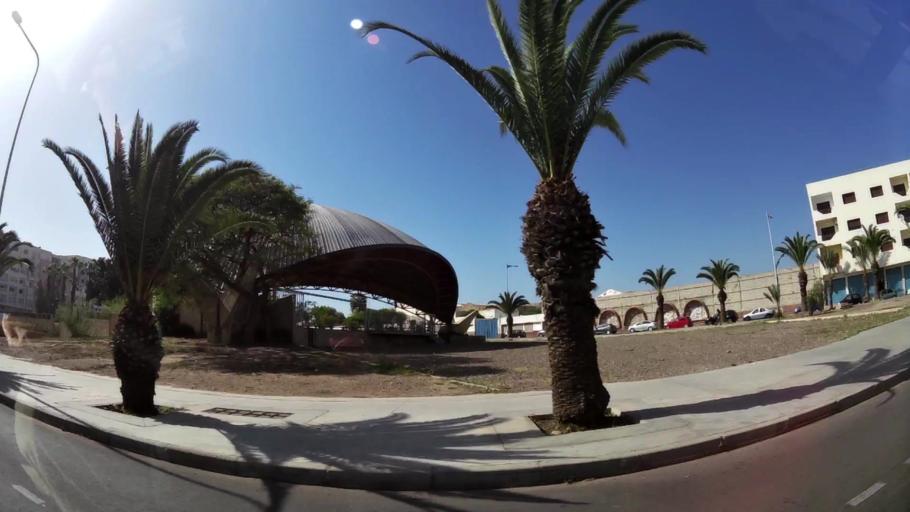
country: MA
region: Souss-Massa-Draa
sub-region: Agadir-Ida-ou-Tnan
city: Agadir
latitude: 30.4149
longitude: -9.5841
